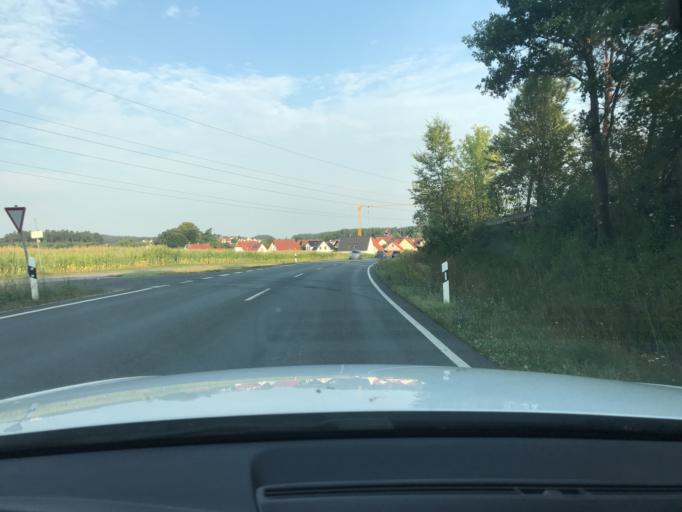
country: DE
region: Bavaria
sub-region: Regierungsbezirk Mittelfranken
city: Schnaittach
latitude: 49.5674
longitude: 11.3186
